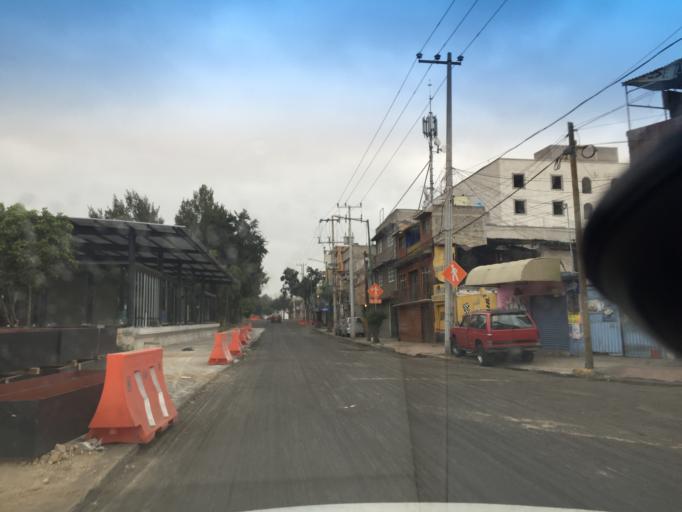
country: MX
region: Mexico City
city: Venustiano Carranza
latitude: 19.4675
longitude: -99.0806
